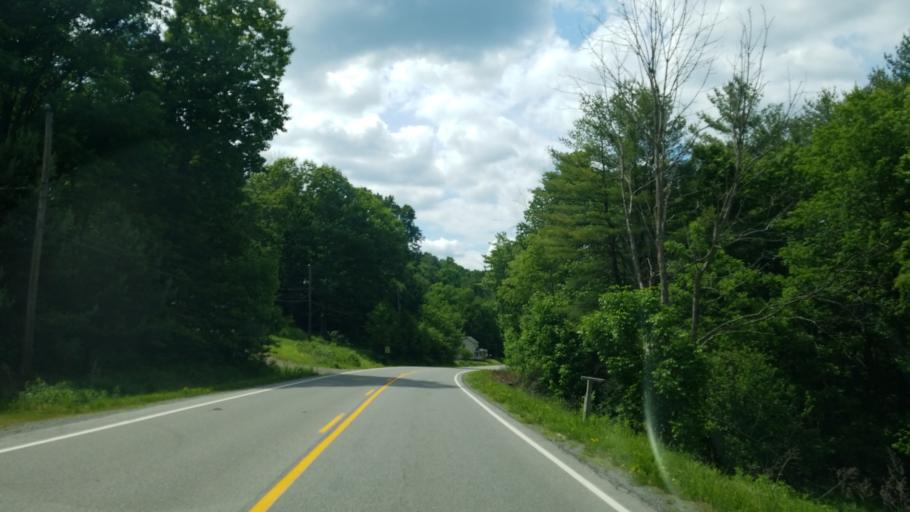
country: US
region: Pennsylvania
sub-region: Clearfield County
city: Clearfield
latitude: 40.9757
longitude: -78.3862
